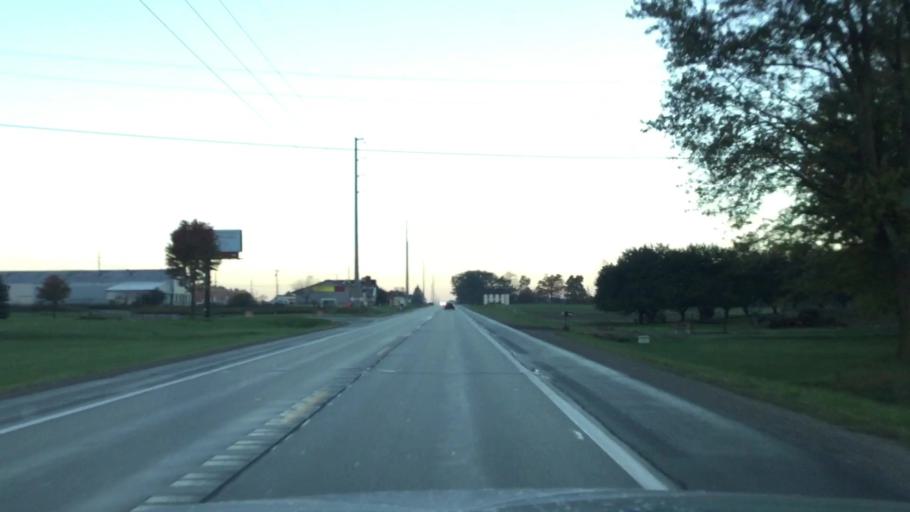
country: US
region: Michigan
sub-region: Livingston County
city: Howell
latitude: 42.6305
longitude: -83.8400
